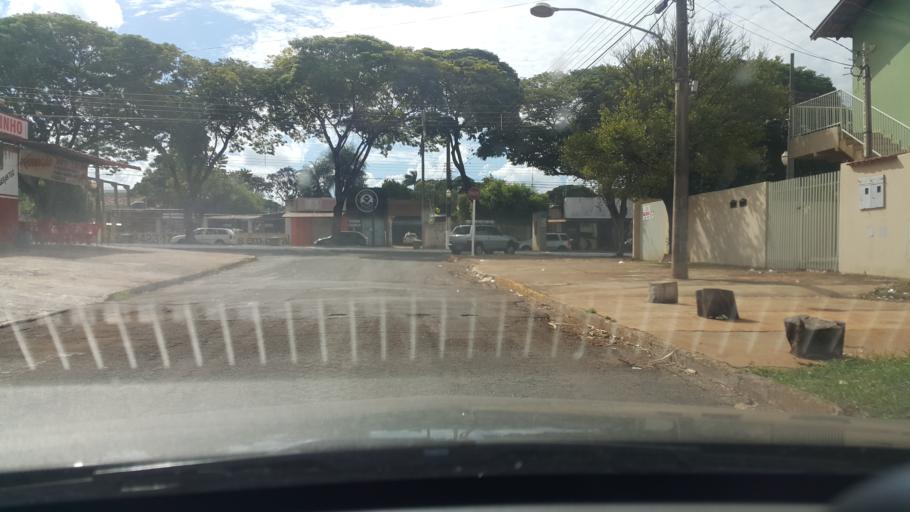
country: BR
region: Mato Grosso do Sul
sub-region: Dourados
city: Dourados
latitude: -22.2334
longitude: -54.8142
